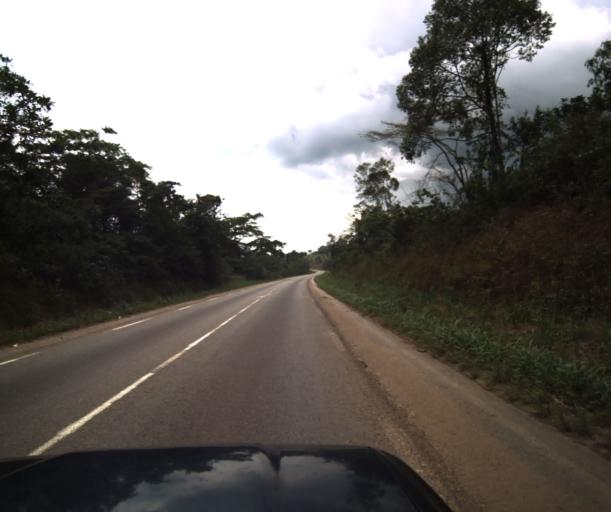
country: CM
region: Littoral
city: Dizangue
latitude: 3.9497
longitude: 10.0188
